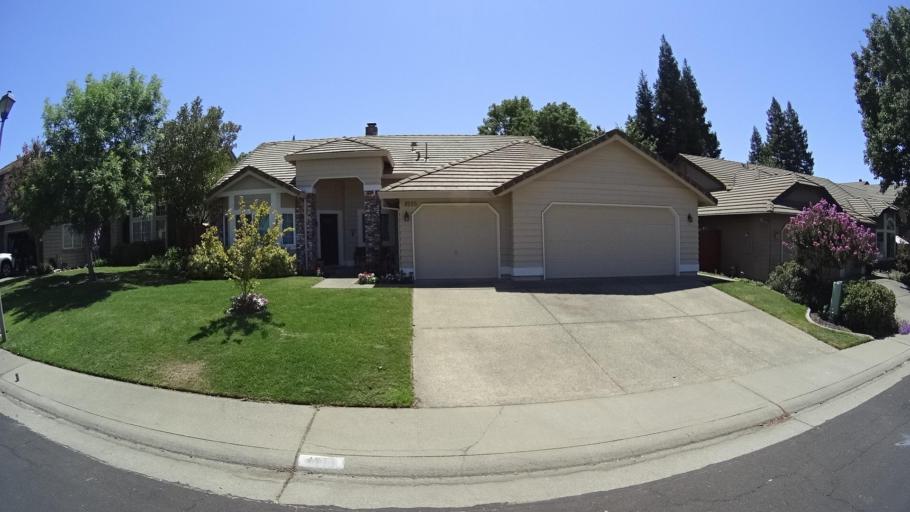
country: US
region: California
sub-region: Placer County
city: Rocklin
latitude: 38.8251
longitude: -121.2553
